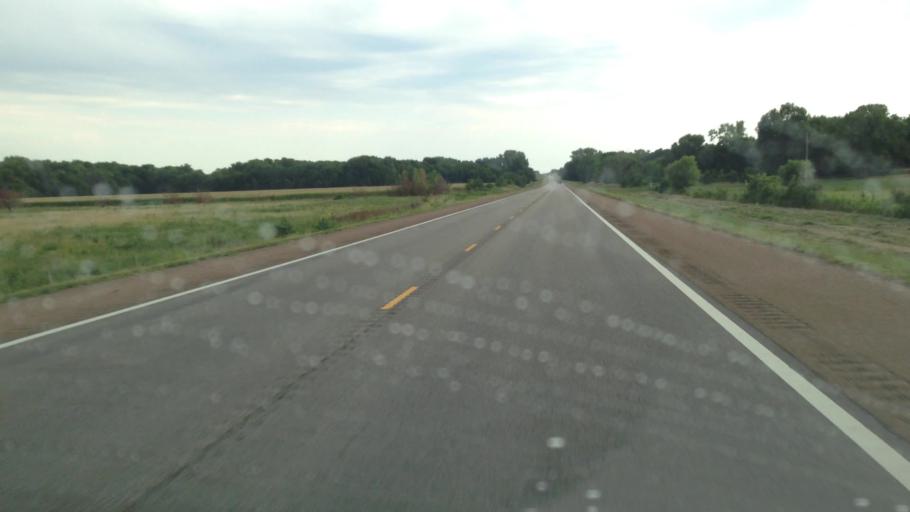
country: US
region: Kansas
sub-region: Woodson County
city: Yates Center
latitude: 38.0341
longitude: -95.7390
